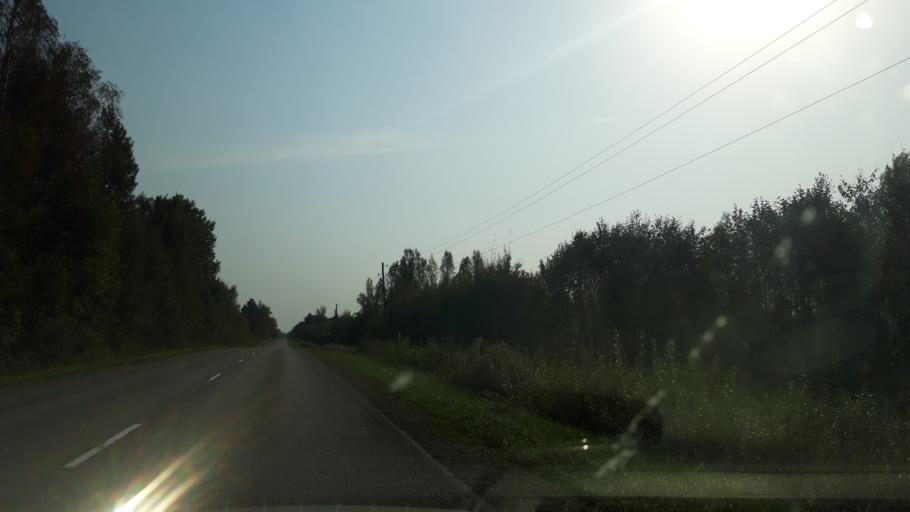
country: LV
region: Burtnieki
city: Matisi
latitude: 57.6491
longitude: 25.2386
